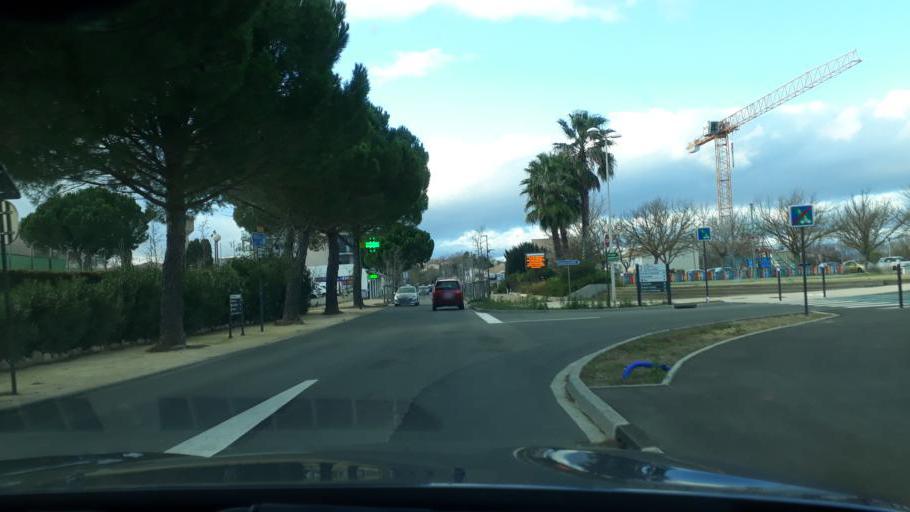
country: FR
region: Languedoc-Roussillon
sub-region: Departement de l'Herault
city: Colombiers
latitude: 43.3124
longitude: 3.1447
